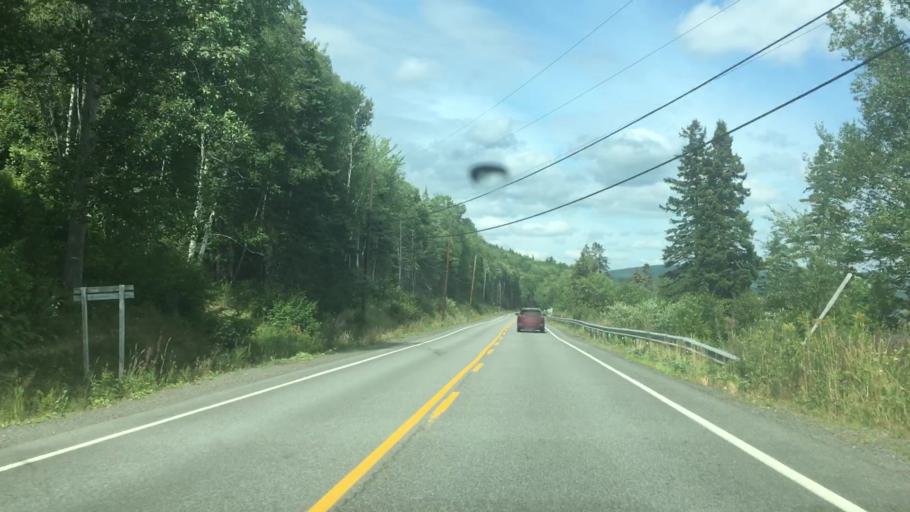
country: CA
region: Nova Scotia
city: Sydney Mines
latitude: 46.2734
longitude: -60.6101
